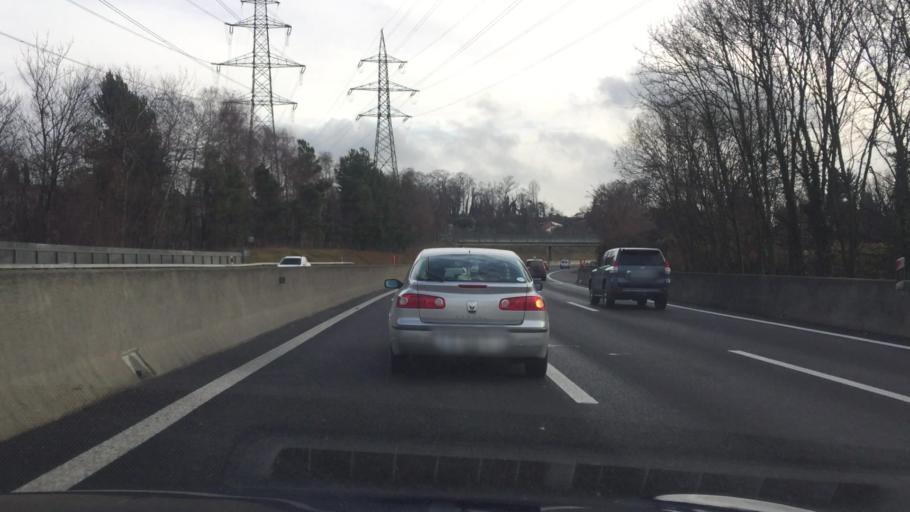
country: CH
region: Vaud
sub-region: Lausanne District
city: Romanel
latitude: 46.5602
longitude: 6.5927
